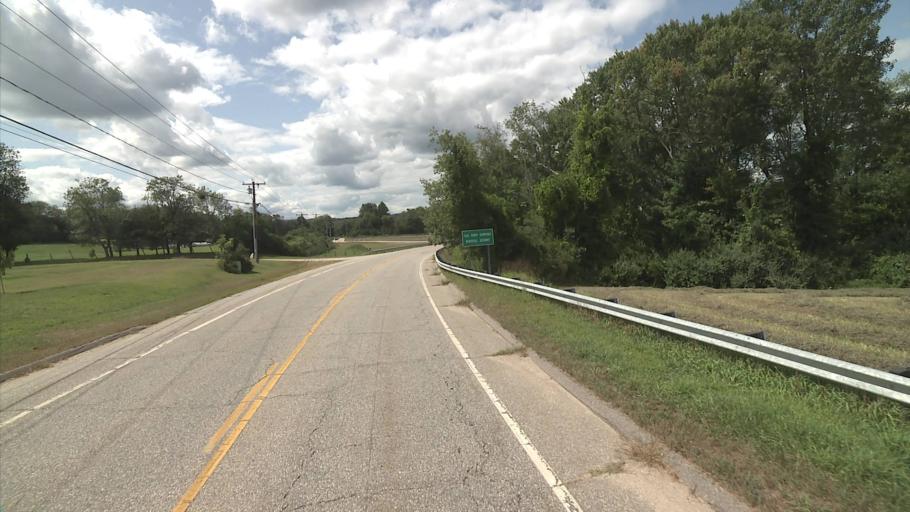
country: US
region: Connecticut
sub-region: New London County
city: Baltic
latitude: 41.6178
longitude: -72.1144
